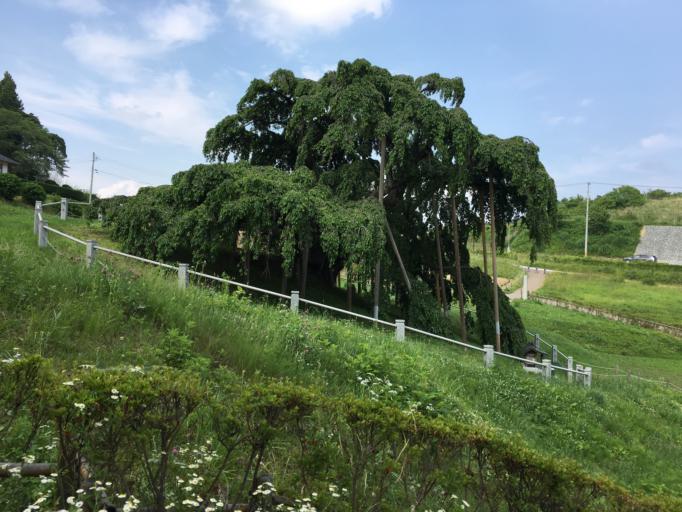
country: JP
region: Fukushima
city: Miharu
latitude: 37.4075
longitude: 140.4998
